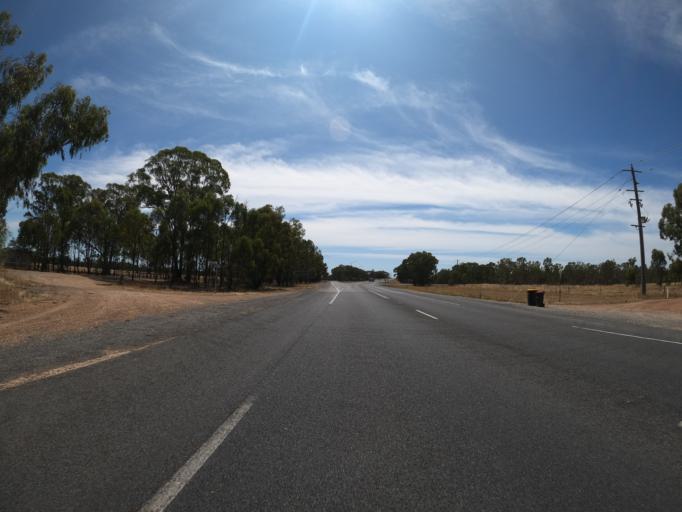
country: AU
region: Victoria
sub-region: Benalla
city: Benalla
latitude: -36.5234
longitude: 146.0572
